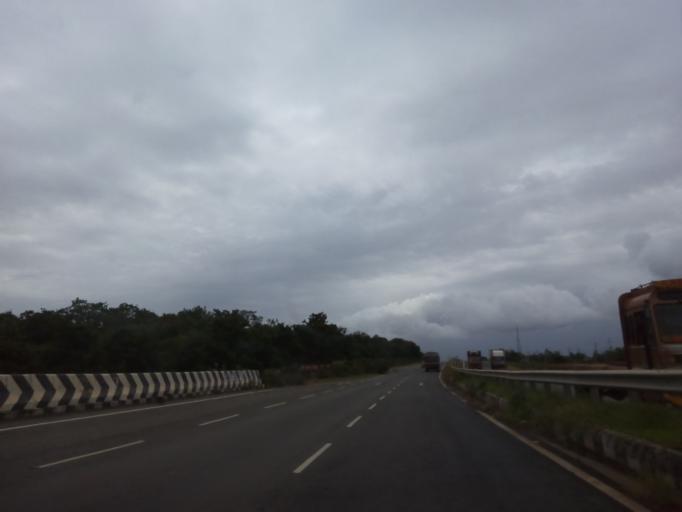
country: IN
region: Karnataka
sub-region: Haveri
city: Ranibennur
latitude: 14.5836
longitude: 75.6744
